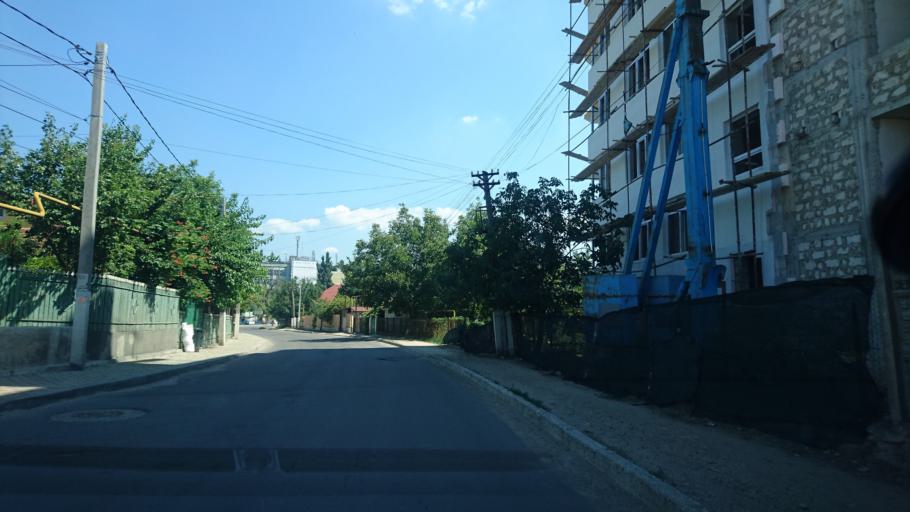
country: MD
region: Chisinau
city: Vatra
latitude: 47.0252
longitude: 28.7704
